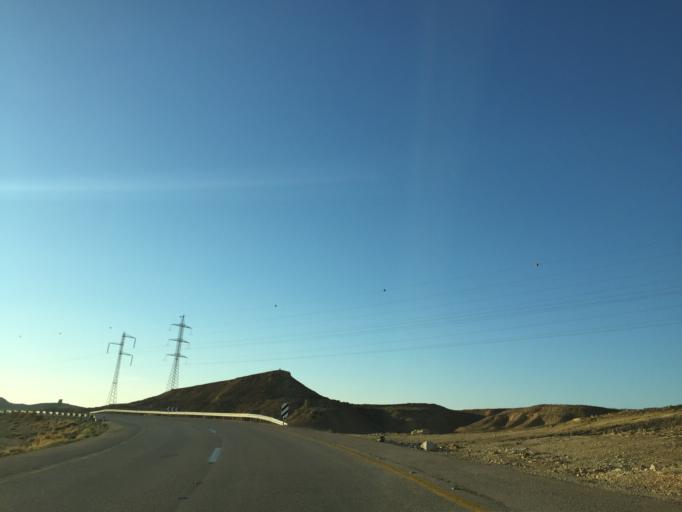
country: IL
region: Southern District
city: Mitzpe Ramon
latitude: 30.5327
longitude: 34.9190
